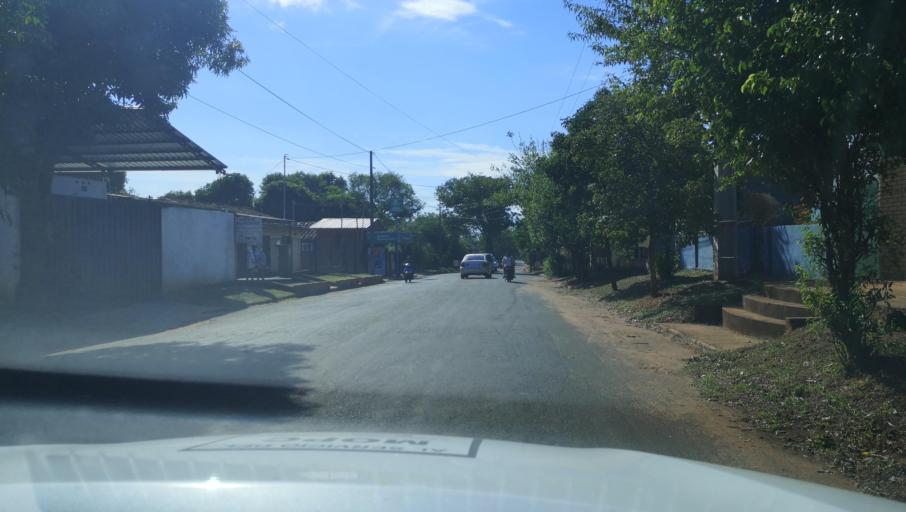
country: PY
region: Misiones
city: Santa Maria
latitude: -26.8933
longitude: -57.0283
